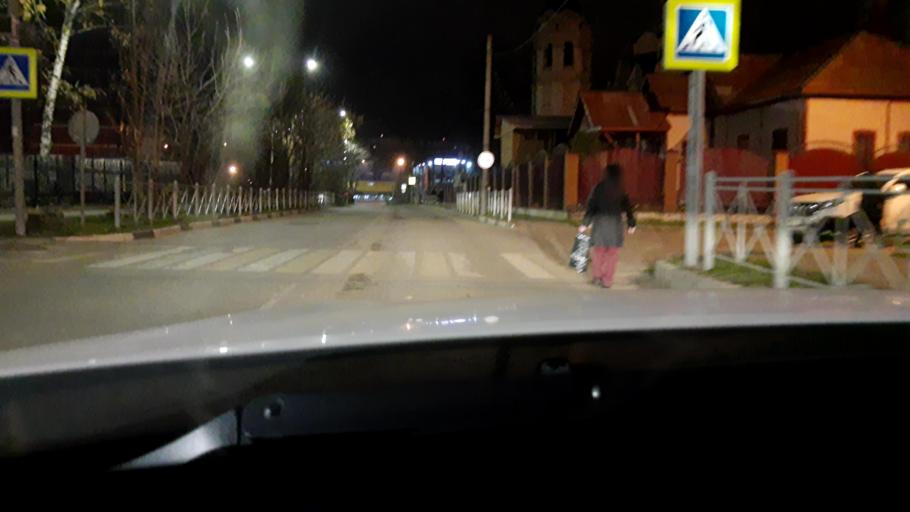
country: RU
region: Moskovskaya
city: Saltykovka
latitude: 55.7492
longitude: 37.9517
